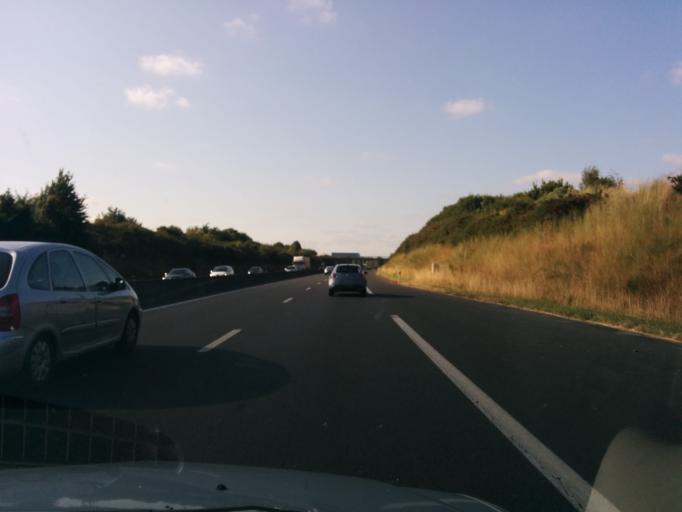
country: FR
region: Pays de la Loire
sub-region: Departement de la Loire-Atlantique
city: Sainte-Luce-sur-Loire
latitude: 47.2593
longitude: -1.4799
